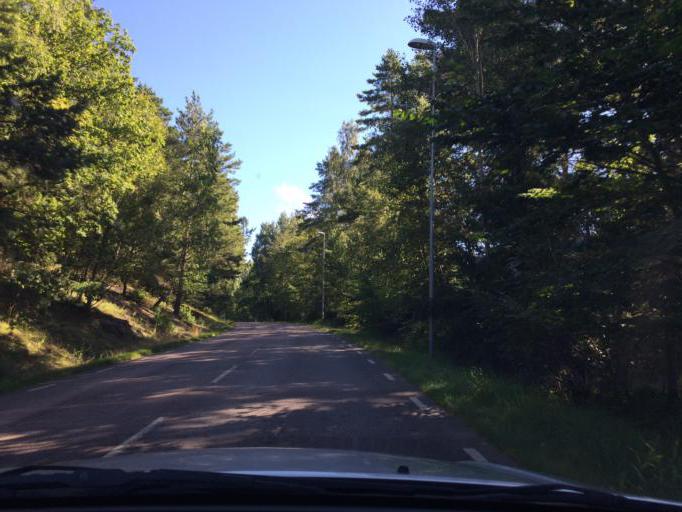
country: SE
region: Vaestmanland
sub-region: Vasteras
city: Vasteras
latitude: 59.5824
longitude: 16.6167
